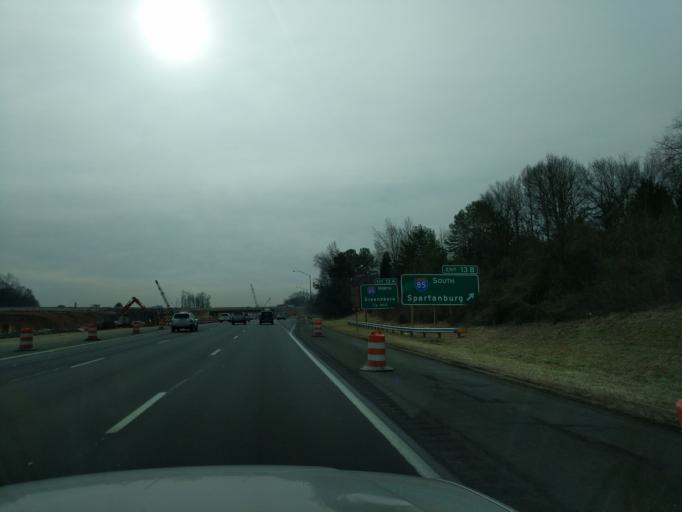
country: US
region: North Carolina
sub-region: Mecklenburg County
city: Charlotte
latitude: 35.2807
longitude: -80.8474
